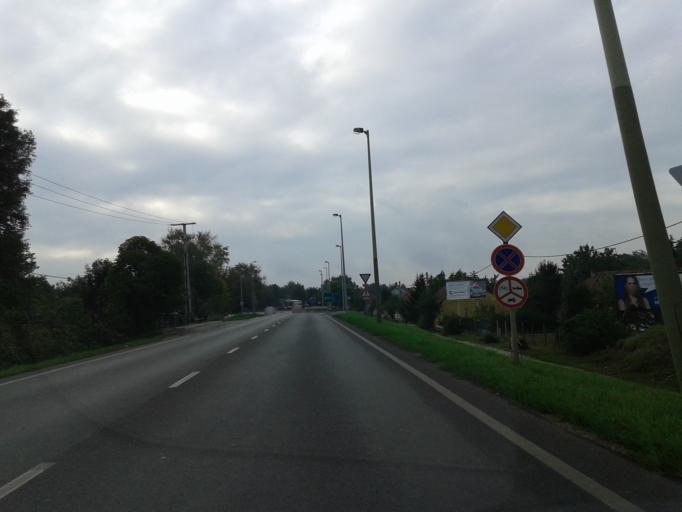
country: HU
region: Csongrad
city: Szeged
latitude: 46.2366
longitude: 20.1703
